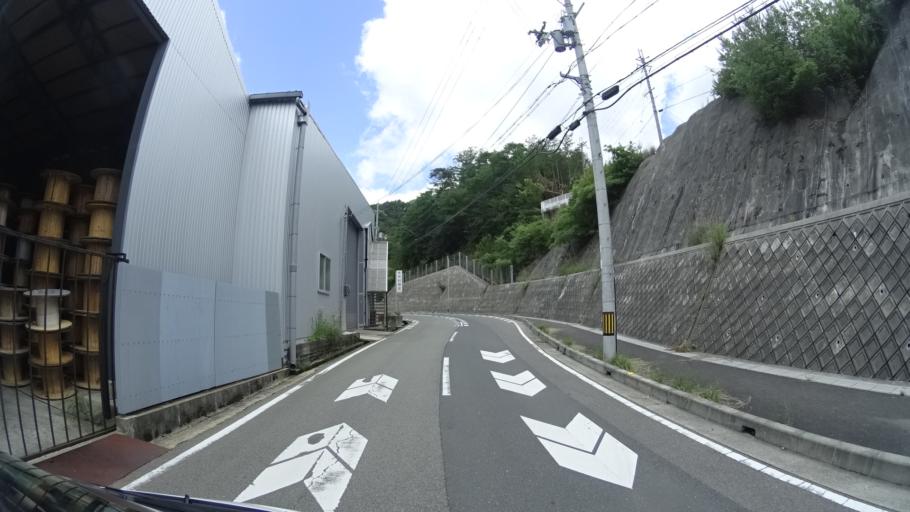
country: JP
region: Kyoto
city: Kameoka
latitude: 35.0163
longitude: 135.4225
